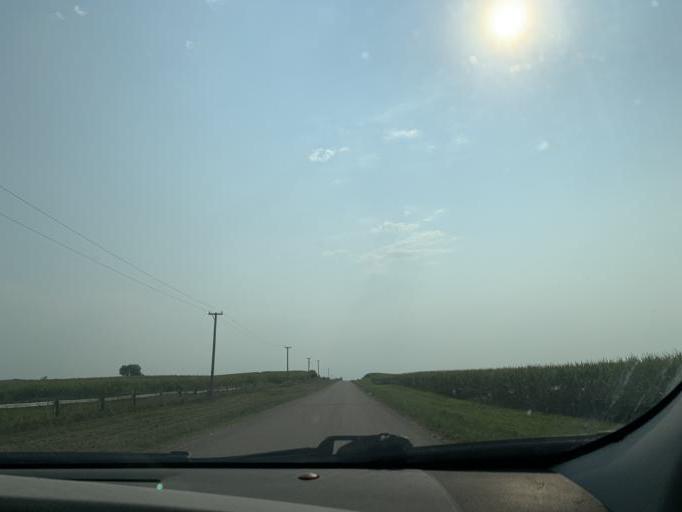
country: US
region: Illinois
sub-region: Whiteside County
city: Morrison
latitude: 41.8697
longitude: -89.9193
